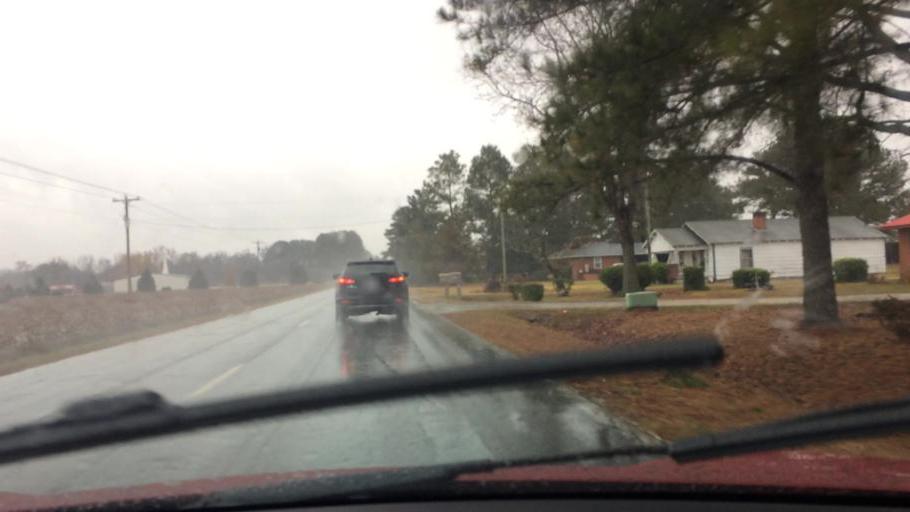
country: US
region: North Carolina
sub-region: Wayne County
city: Elroy
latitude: 35.4082
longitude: -77.9276
